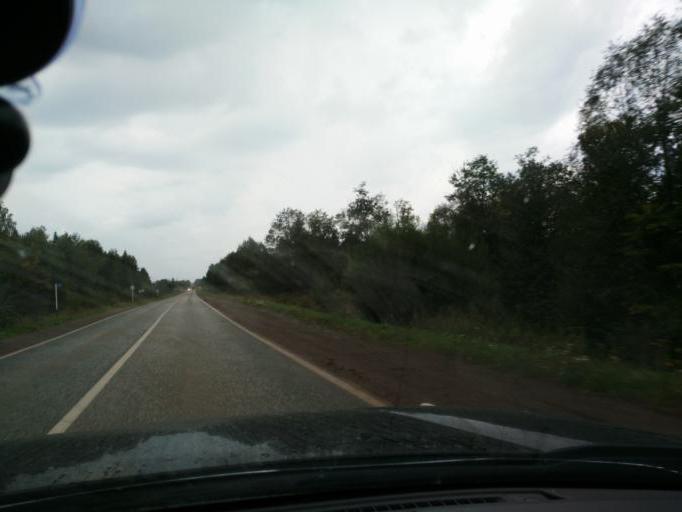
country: RU
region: Perm
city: Barda
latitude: 56.8529
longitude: 55.9400
